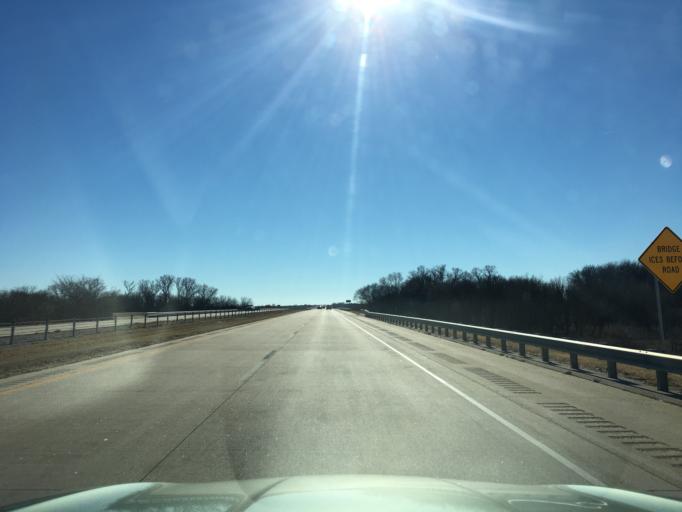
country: US
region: Oklahoma
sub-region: Noble County
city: Perry
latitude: 36.4791
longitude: -97.3272
